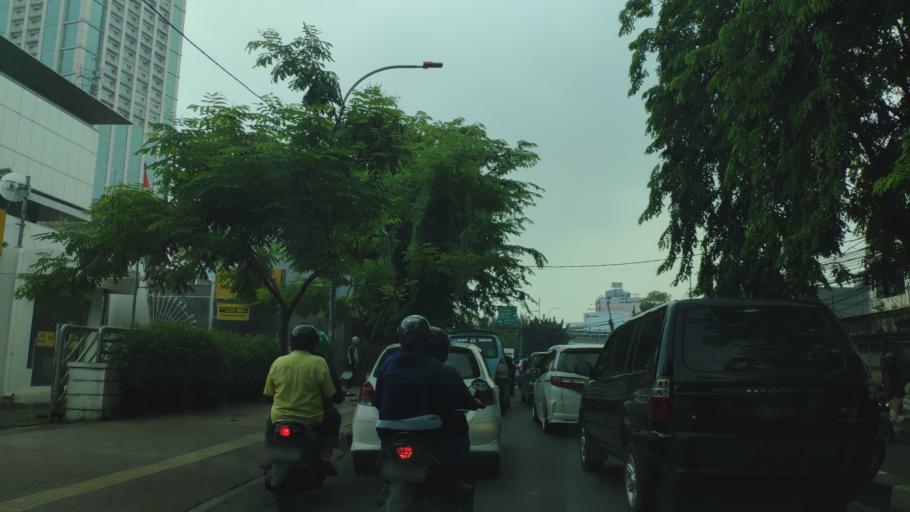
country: ID
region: Jakarta Raya
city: Jakarta
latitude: -6.2028
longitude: 106.7980
